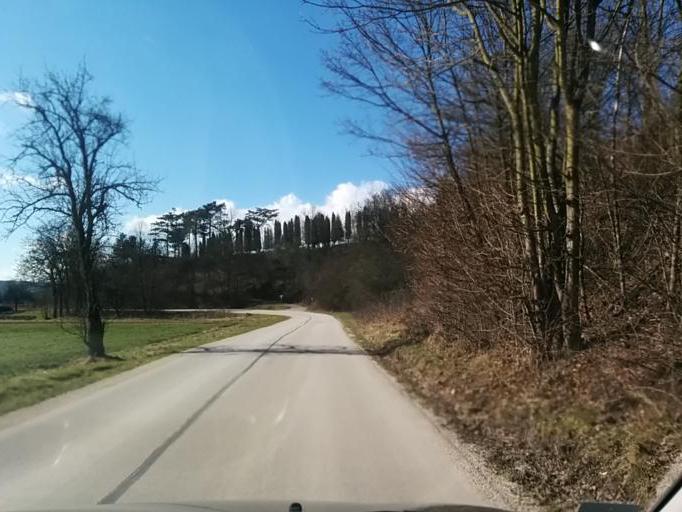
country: SK
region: Nitriansky
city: Cachtice
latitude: 48.7178
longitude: 17.7324
